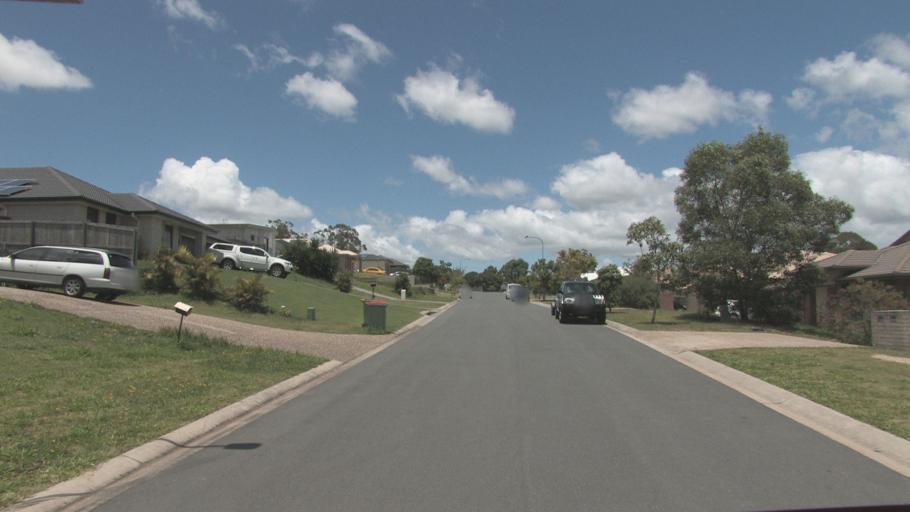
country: AU
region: Queensland
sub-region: Logan
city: Beenleigh
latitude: -27.6960
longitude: 153.2022
